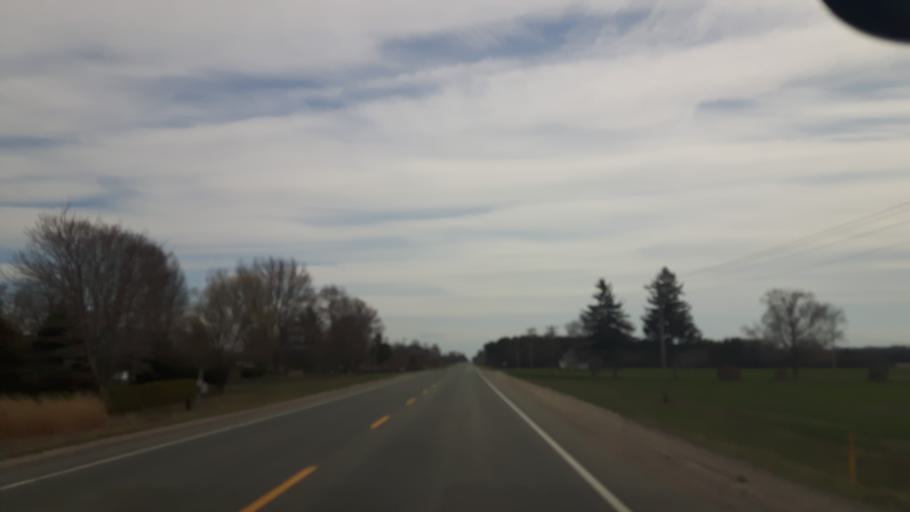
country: CA
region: Ontario
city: Goderich
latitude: 43.7130
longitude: -81.7058
